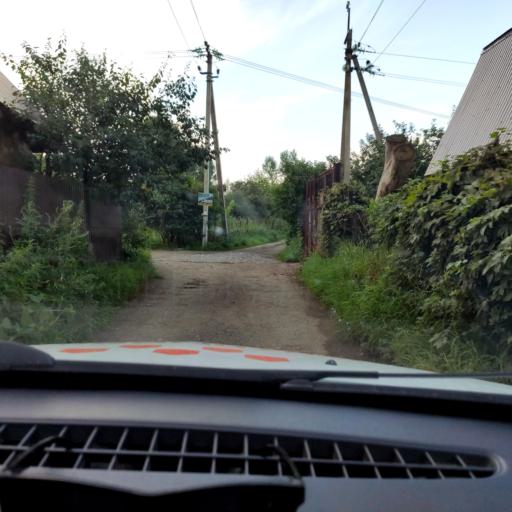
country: RU
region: Bashkortostan
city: Iglino
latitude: 54.7870
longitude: 56.2079
